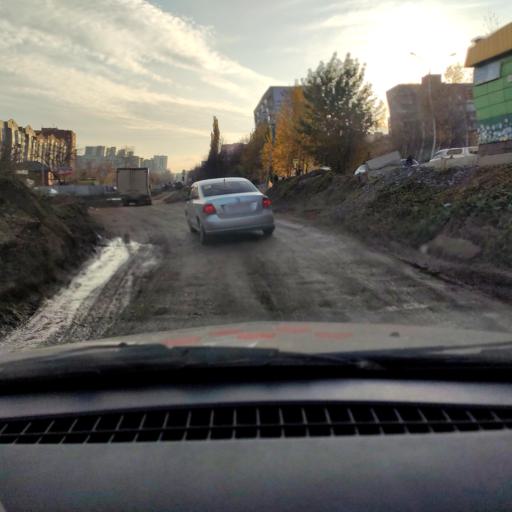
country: RU
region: Bashkortostan
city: Ufa
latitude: 54.7480
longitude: 56.0012
